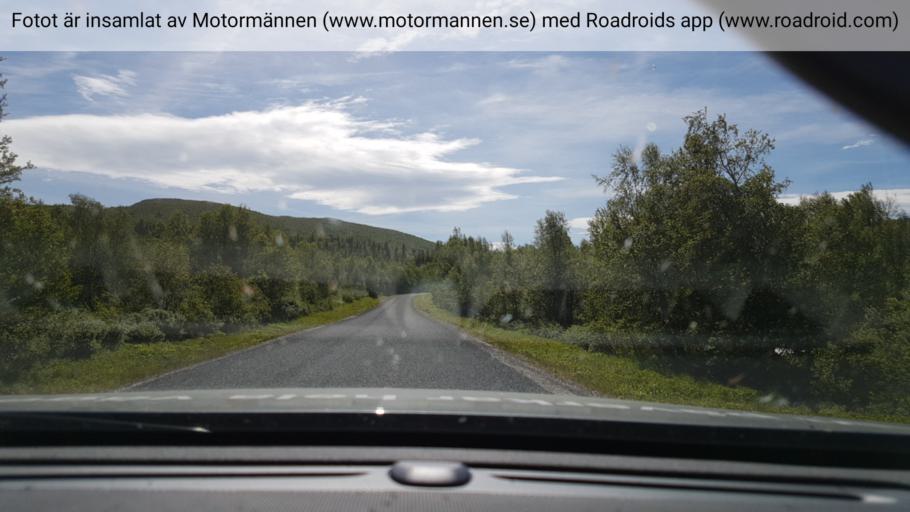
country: SE
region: Vaesterbotten
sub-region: Vilhelmina Kommun
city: Sjoberg
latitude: 65.3166
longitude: 15.2894
